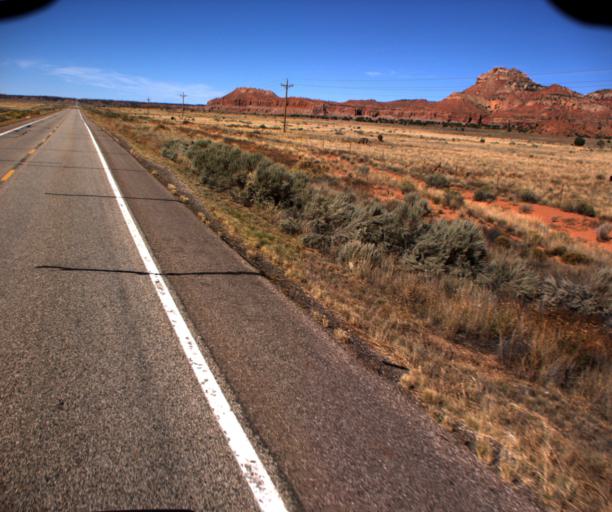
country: US
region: Arizona
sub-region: Mohave County
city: Colorado City
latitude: 36.8640
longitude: -112.8302
